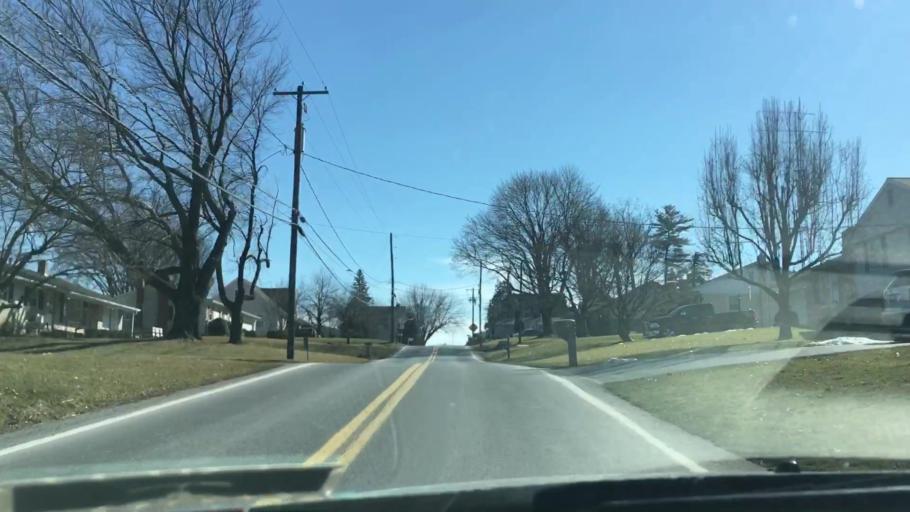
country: US
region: Pennsylvania
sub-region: Lancaster County
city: Brownstown
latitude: 40.0942
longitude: -76.1530
